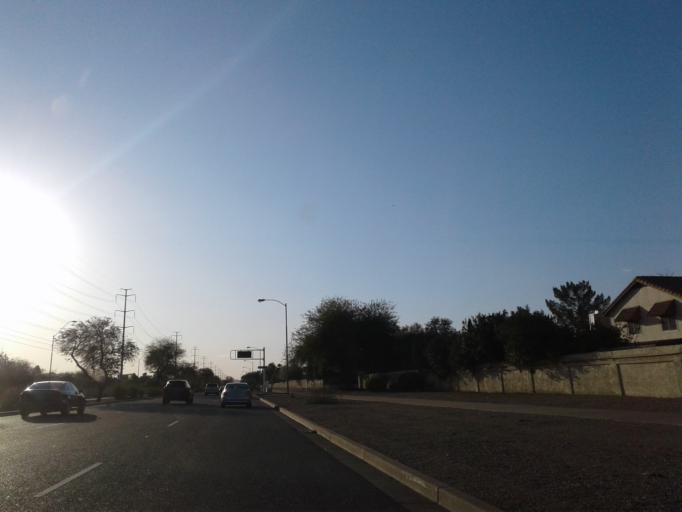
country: US
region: Arizona
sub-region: Maricopa County
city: Scottsdale
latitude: 33.5826
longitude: -111.8599
